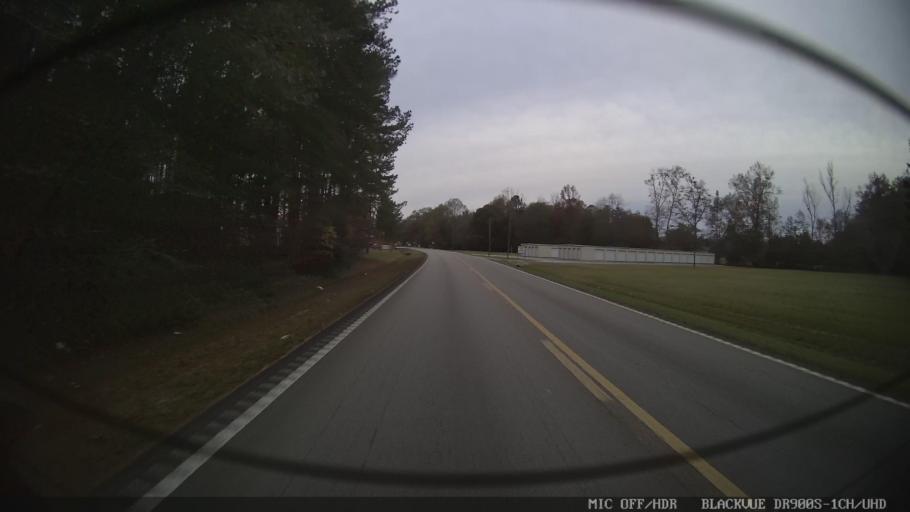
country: US
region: Mississippi
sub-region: Clarke County
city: Stonewall
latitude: 32.0383
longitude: -88.8791
